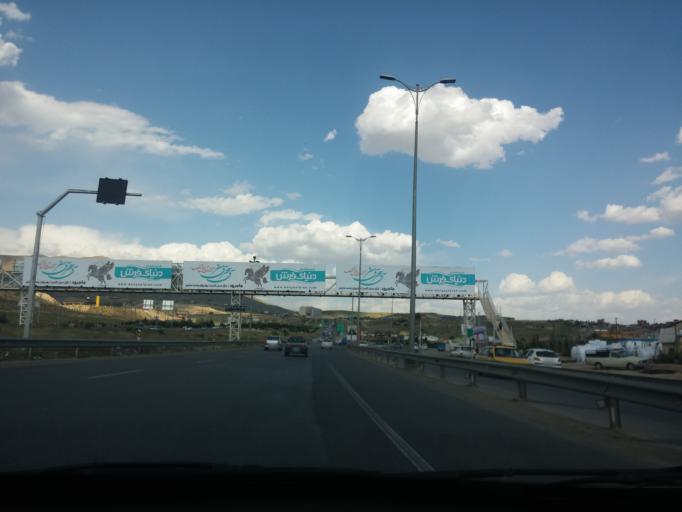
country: IR
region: Tehran
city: Damavand
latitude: 35.7193
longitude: 51.9182
